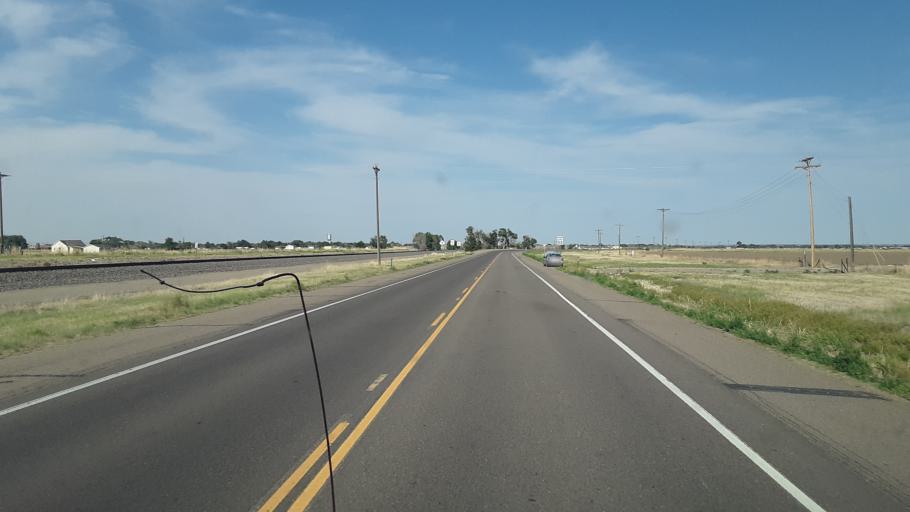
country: US
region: Colorado
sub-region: Bent County
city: Las Animas
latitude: 38.0618
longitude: -103.2538
